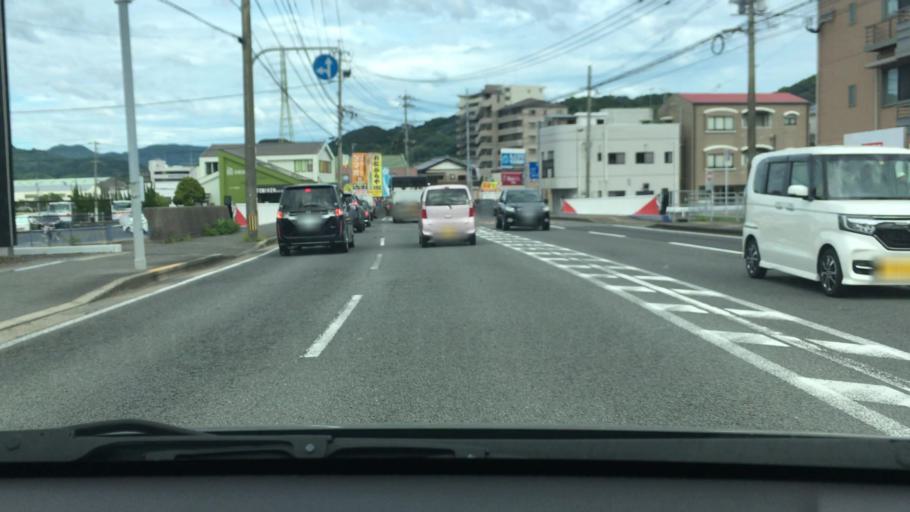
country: JP
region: Nagasaki
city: Togitsu
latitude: 32.8318
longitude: 129.8460
